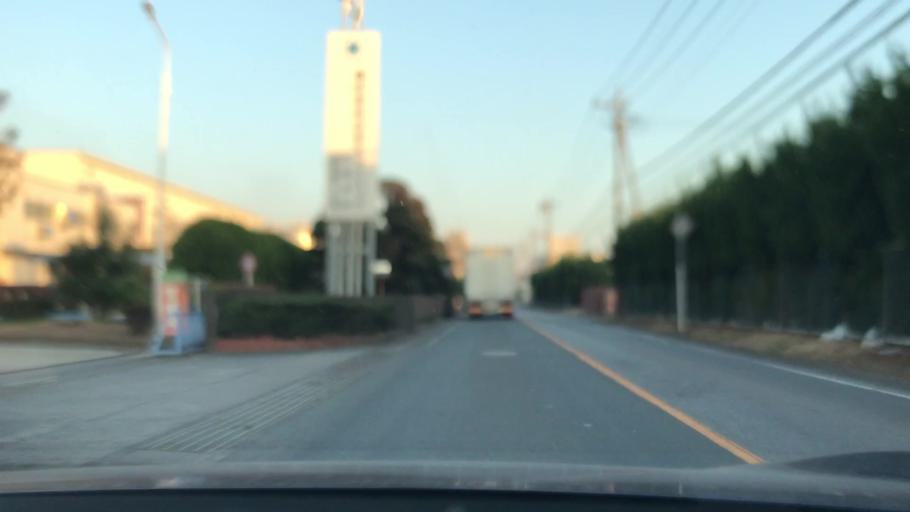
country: JP
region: Saitama
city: Hanyu
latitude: 36.2065
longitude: 139.5050
